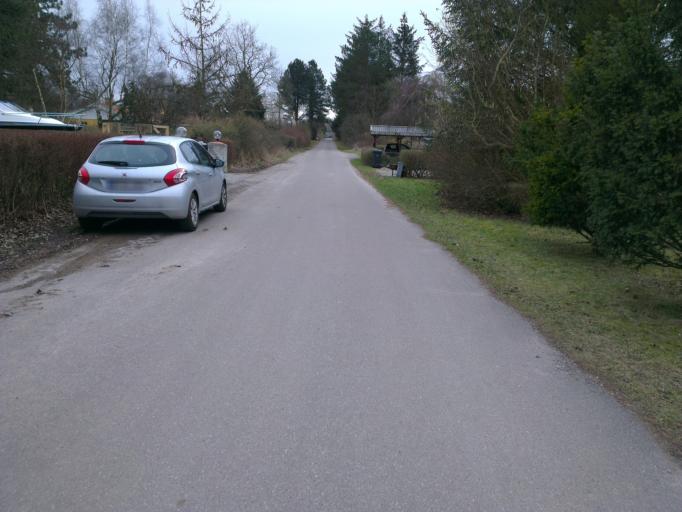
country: DK
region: Capital Region
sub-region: Frederikssund Kommune
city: Jaegerspris
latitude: 55.8189
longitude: 11.9371
